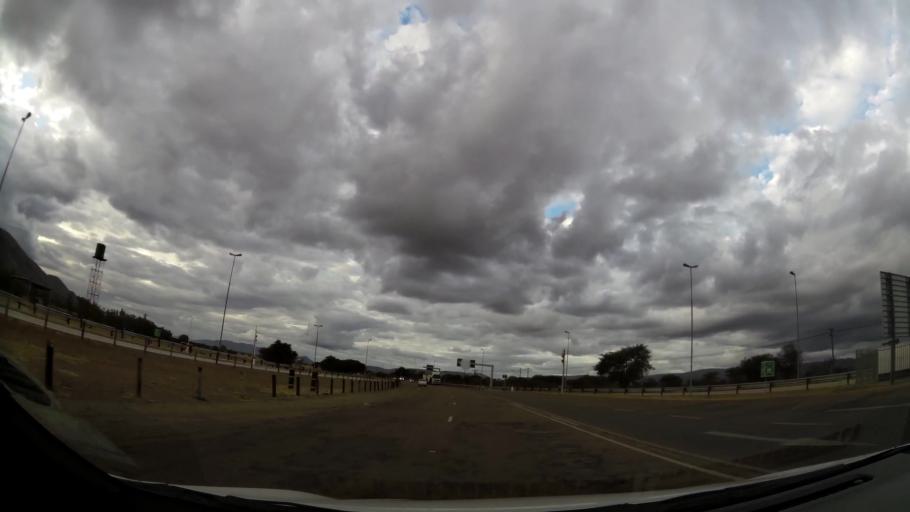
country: ZA
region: Limpopo
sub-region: Waterberg District Municipality
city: Mokopane
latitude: -24.2734
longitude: 28.9799
